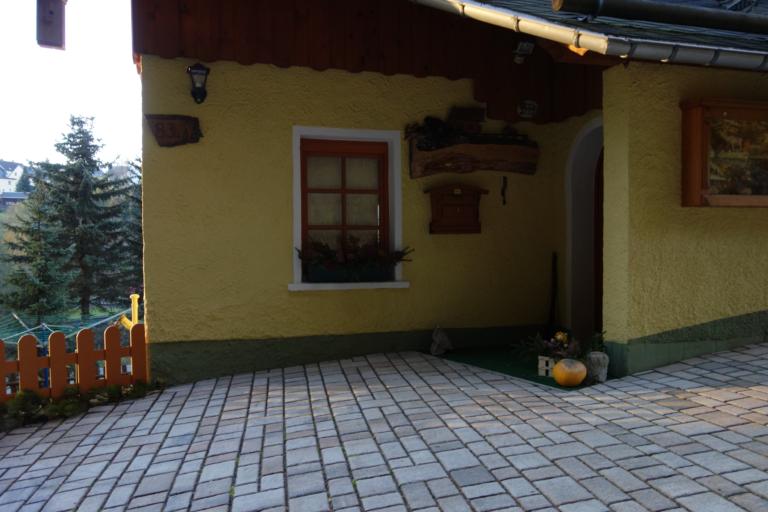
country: DE
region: Saxony
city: Johstadt
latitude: 50.5096
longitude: 13.1003
